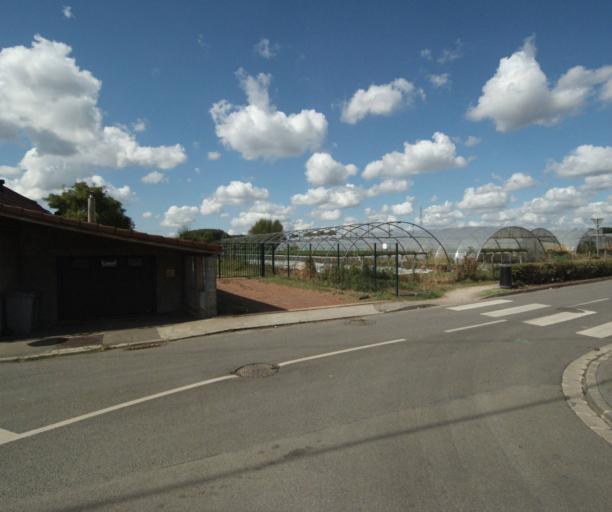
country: FR
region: Nord-Pas-de-Calais
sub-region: Departement du Nord
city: Willems
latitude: 50.6253
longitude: 3.2297
